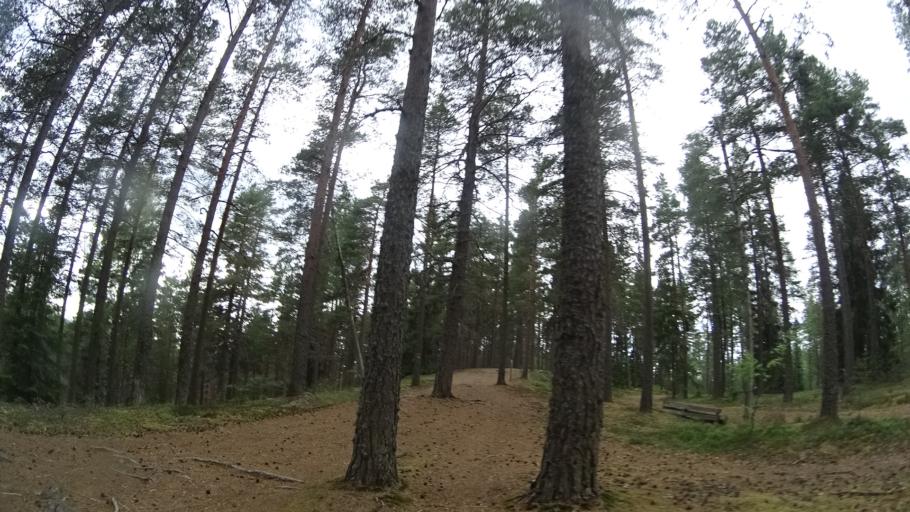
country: FI
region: Satakunta
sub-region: Pohjois-Satakunta
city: Jaemijaervi
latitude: 61.7725
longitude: 22.7350
